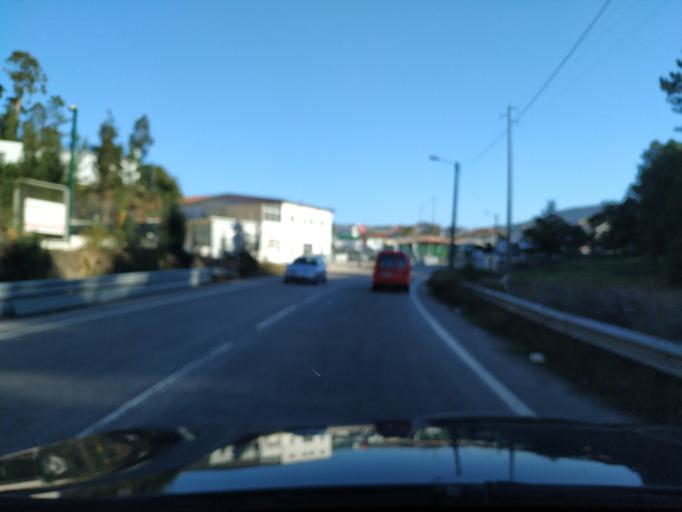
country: PT
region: Aveiro
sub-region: Oliveira de Azemeis
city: Vila Cha
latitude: 40.8790
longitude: -8.4283
